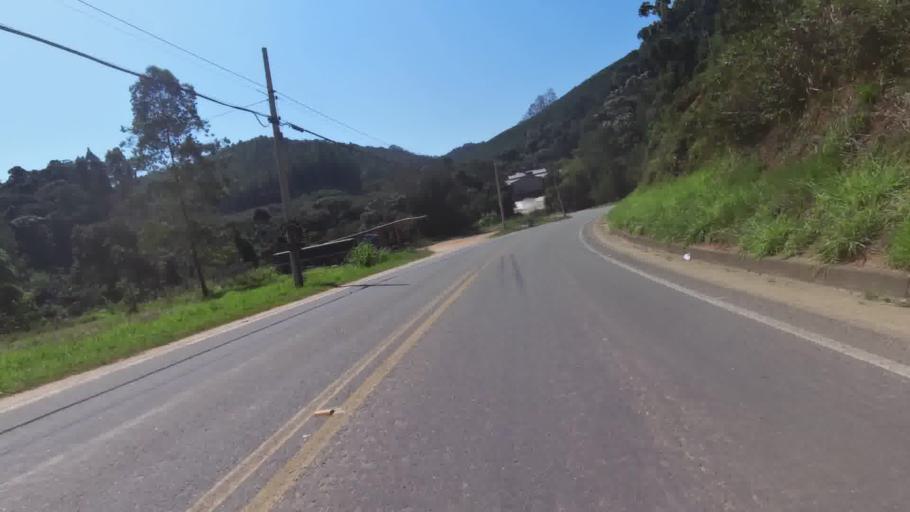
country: BR
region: Espirito Santo
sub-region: Marechal Floriano
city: Marechal Floriano
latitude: -20.4479
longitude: -40.7864
